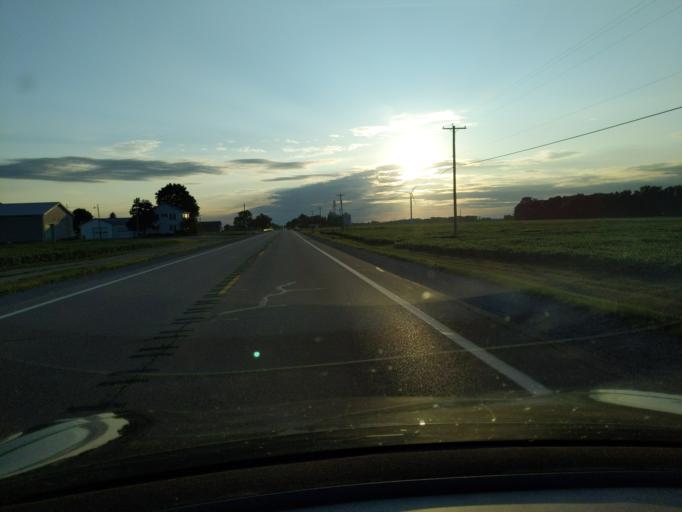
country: US
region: Michigan
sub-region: Gratiot County
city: Breckenridge
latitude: 43.4080
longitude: -84.5342
